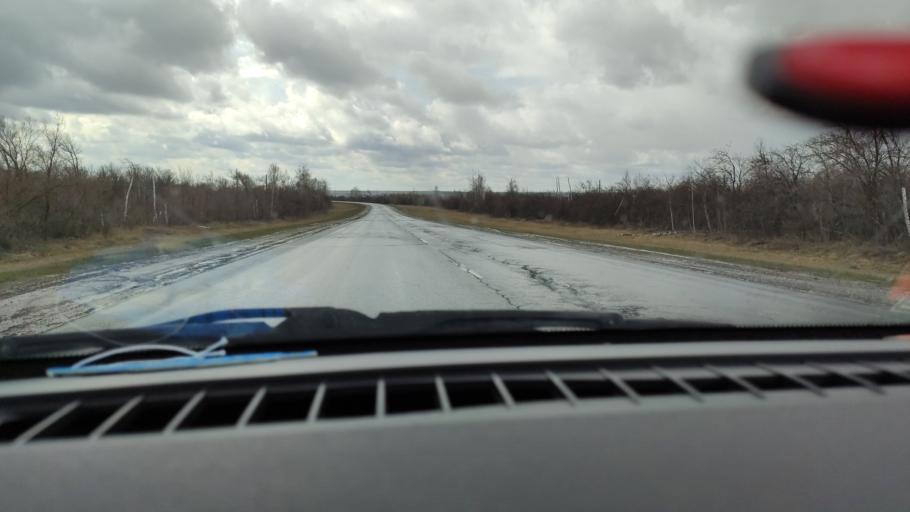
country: RU
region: Samara
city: Yelkhovka
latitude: 53.9263
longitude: 50.2610
